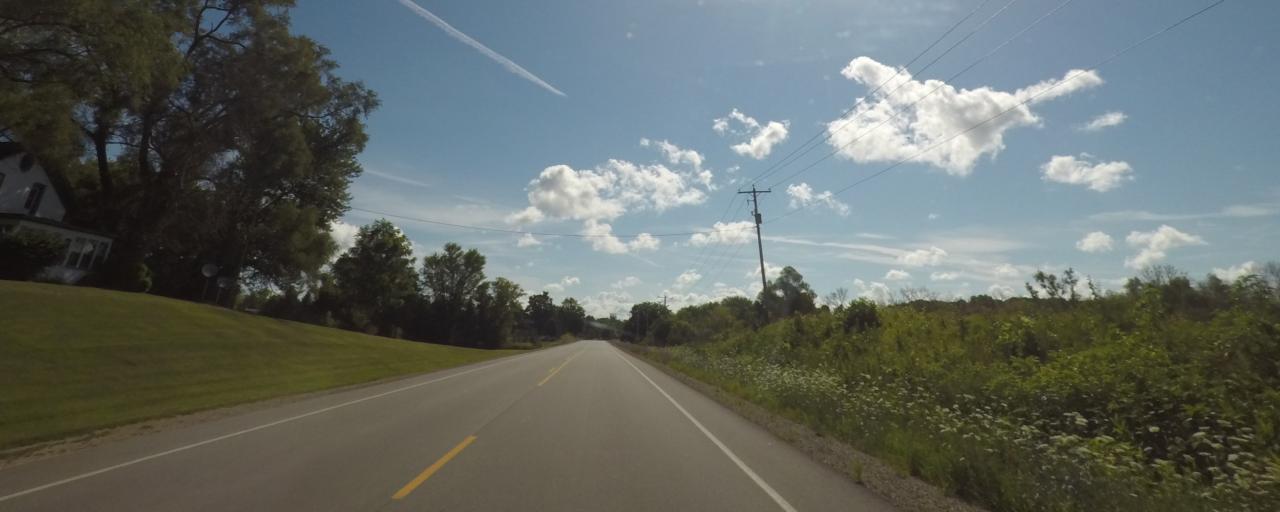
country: US
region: Wisconsin
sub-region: Jefferson County
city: Ixonia
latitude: 43.0685
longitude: -88.6065
